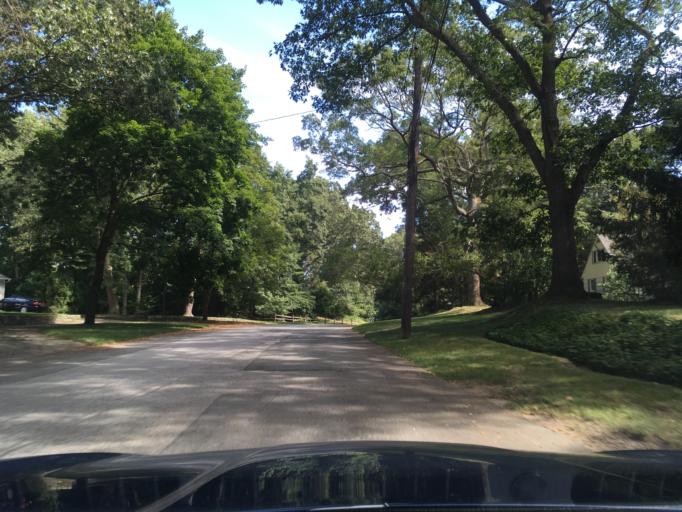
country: US
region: Rhode Island
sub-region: Kent County
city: East Greenwich
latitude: 41.6576
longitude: -71.4707
